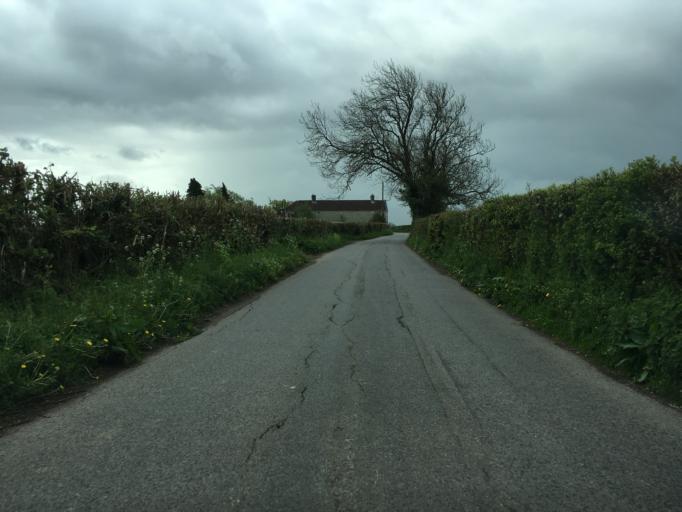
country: GB
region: England
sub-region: Bath and North East Somerset
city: Clutton
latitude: 51.3346
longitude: -2.5193
